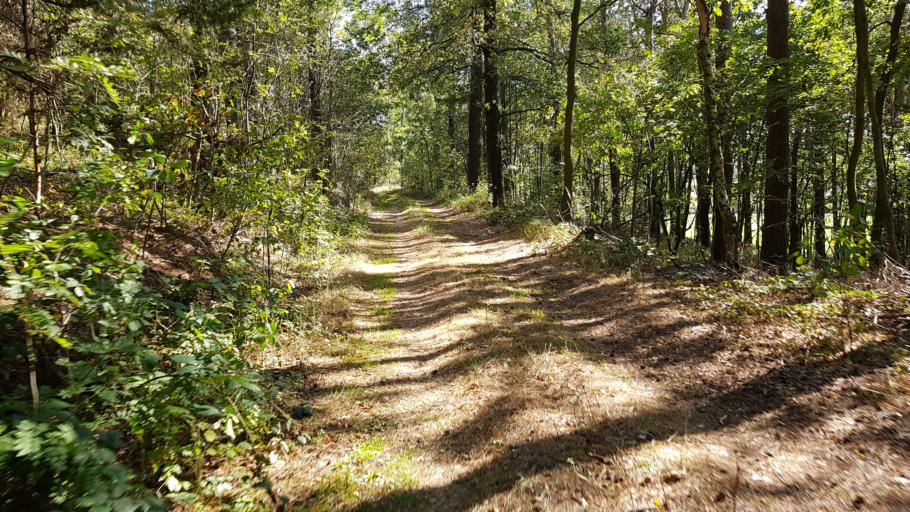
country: DE
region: Saxony
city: Grossnaundorf
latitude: 51.2134
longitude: 13.9601
